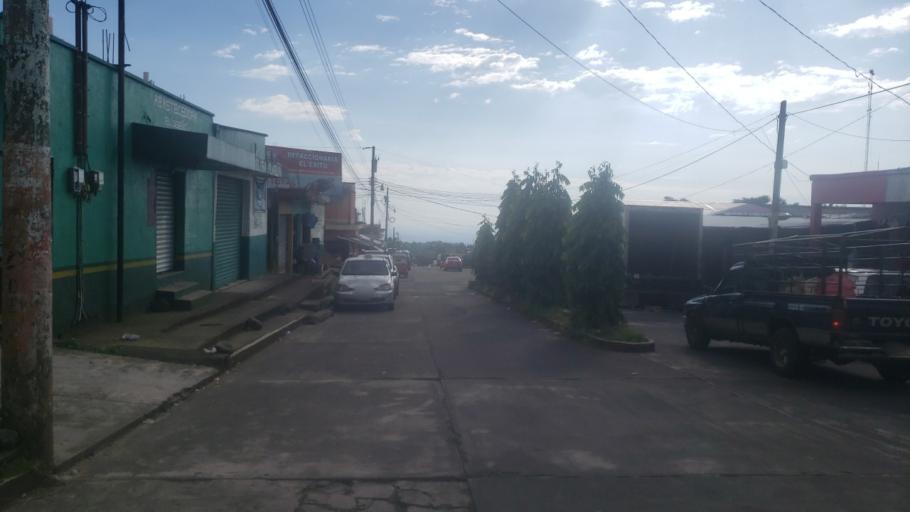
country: GT
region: Suchitepeque
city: Pueblo Nuevo
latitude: 14.6470
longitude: -91.5573
